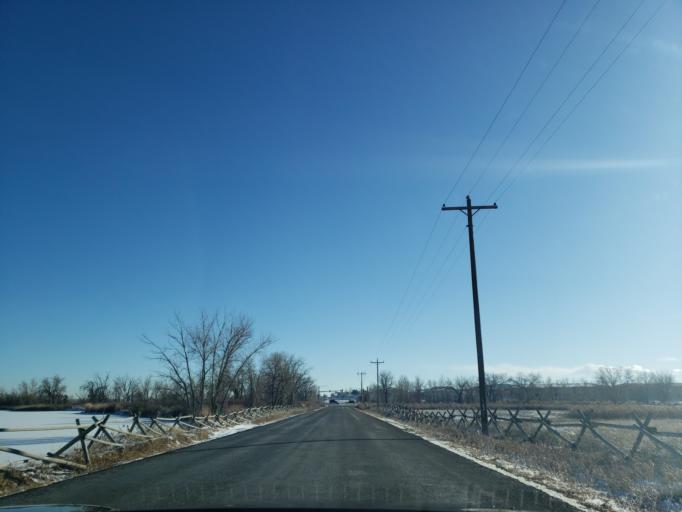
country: US
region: Colorado
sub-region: Larimer County
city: Fort Collins
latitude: 40.5263
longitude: -105.0013
